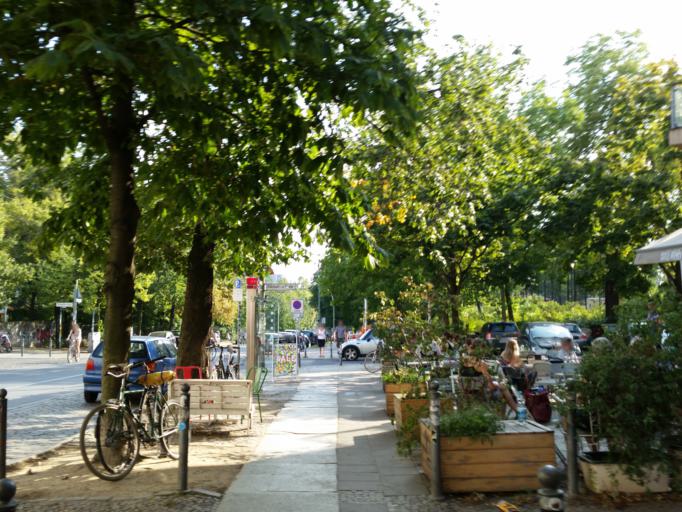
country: DE
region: Berlin
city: Berlin
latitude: 52.5335
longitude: 13.4045
